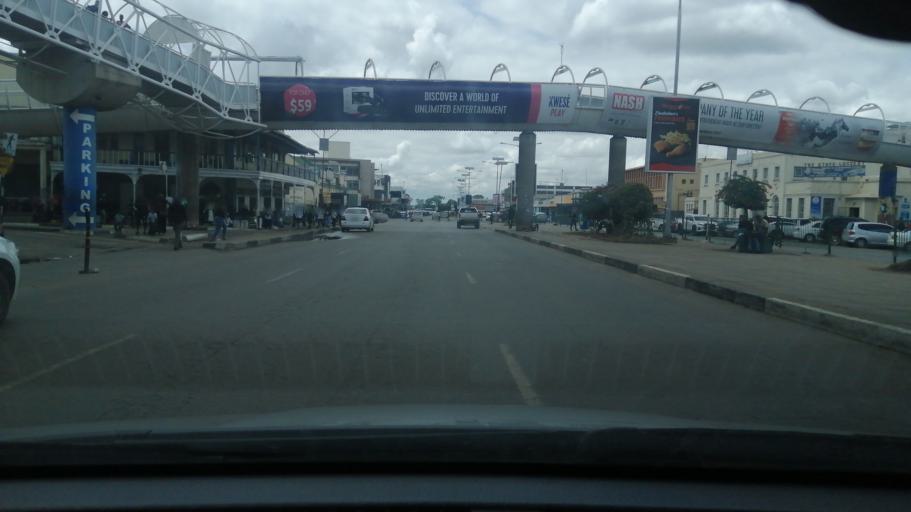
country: ZW
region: Harare
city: Harare
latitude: -17.8320
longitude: 31.0468
